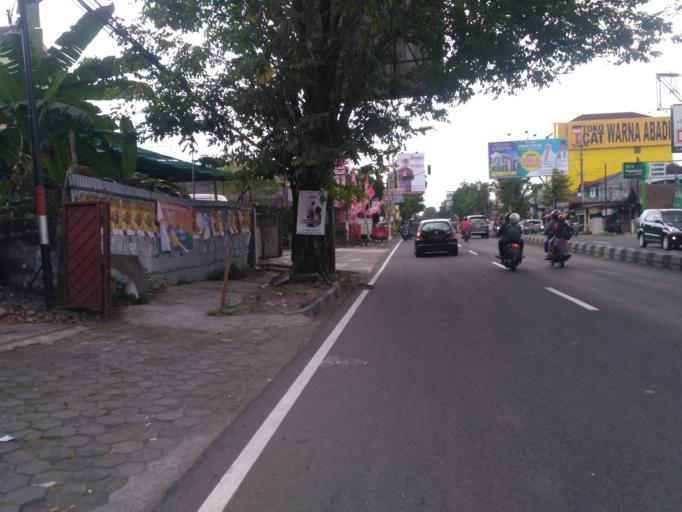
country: ID
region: Daerah Istimewa Yogyakarta
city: Melati
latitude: -7.7416
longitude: 110.3627
